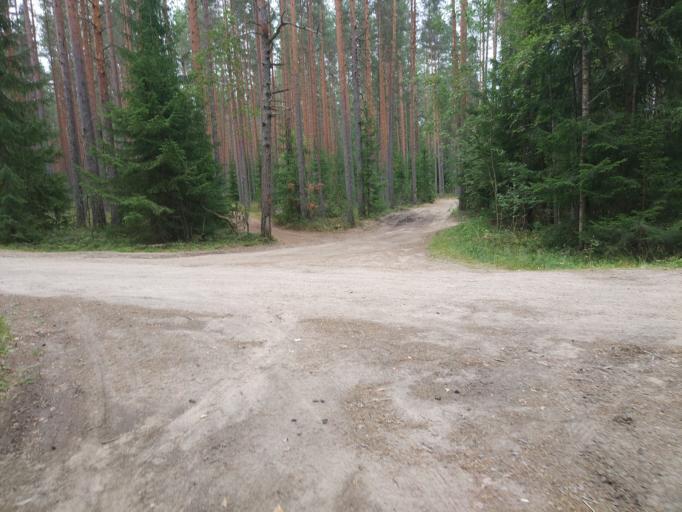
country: RU
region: Leningrad
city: Kuznechnoye
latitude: 61.0106
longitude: 29.6478
